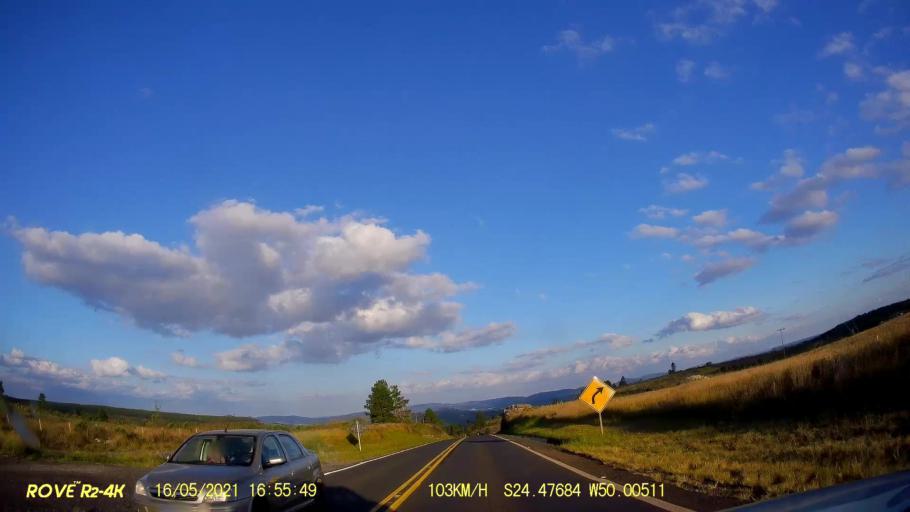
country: BR
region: Parana
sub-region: Pirai Do Sul
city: Pirai do Sul
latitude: -24.4765
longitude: -50.0050
